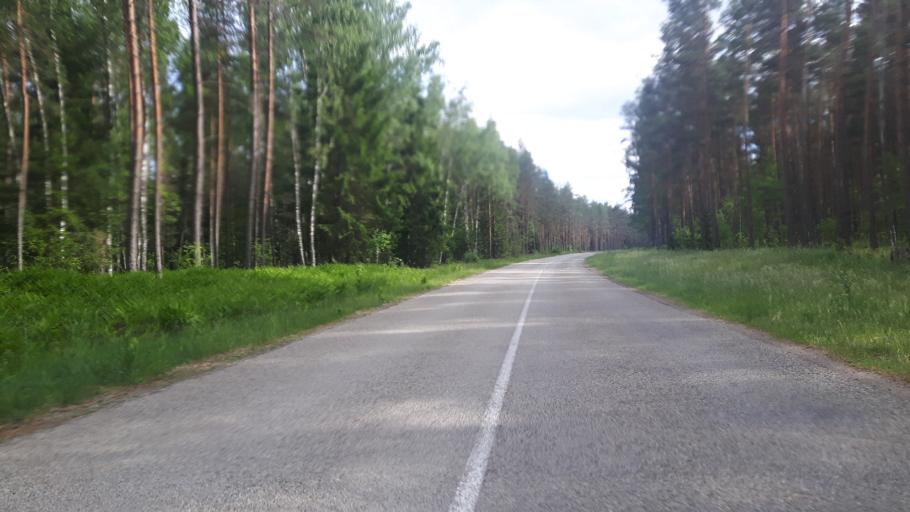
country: LV
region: Engure
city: Smarde
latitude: 57.0221
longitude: 23.3456
